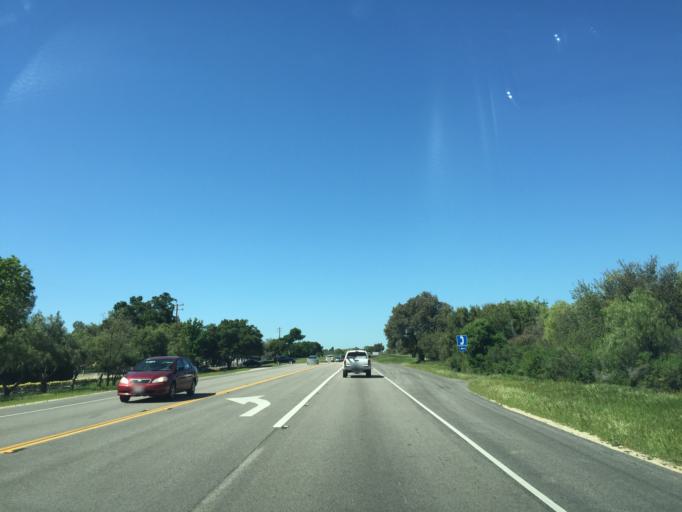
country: US
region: California
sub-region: Santa Barbara County
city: Los Olivos
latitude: 34.6571
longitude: -120.1008
